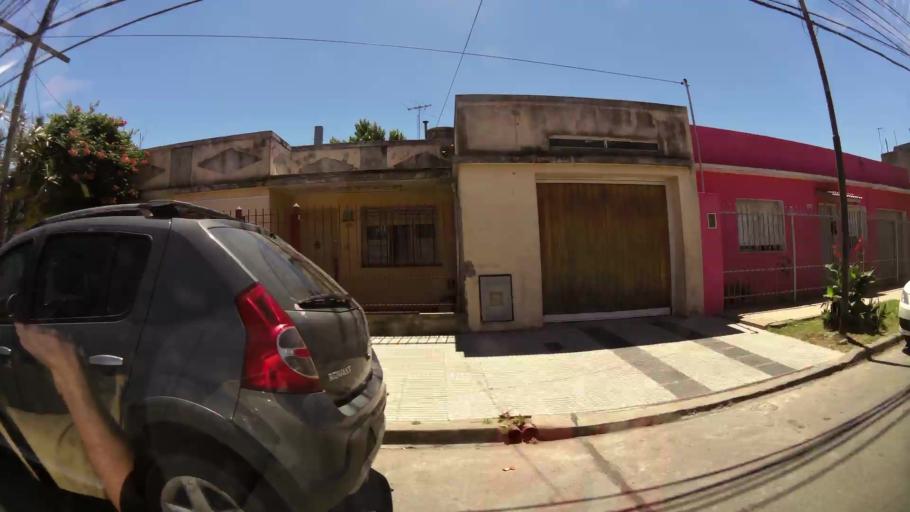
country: AR
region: Buenos Aires
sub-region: Partido de Tigre
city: Tigre
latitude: -34.5026
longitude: -58.5828
